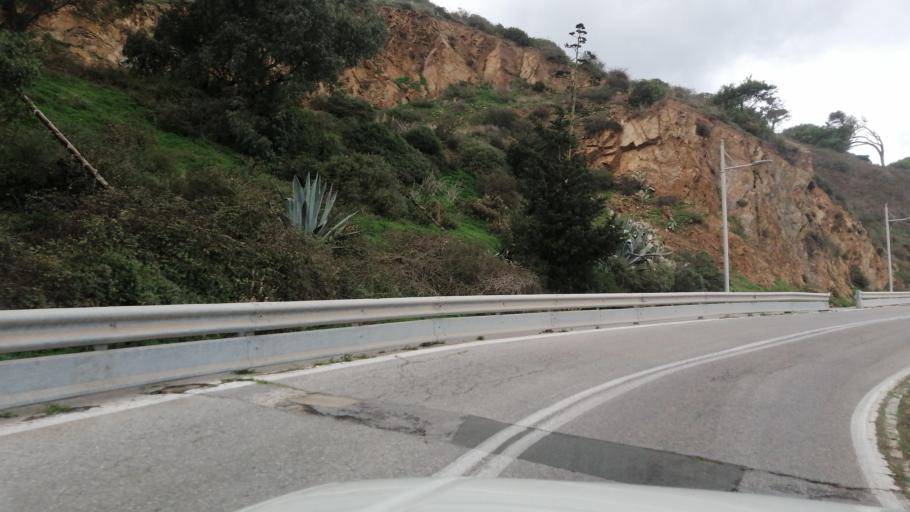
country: ES
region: Ceuta
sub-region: Ceuta
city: Ceuta
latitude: 35.8952
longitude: -5.2861
